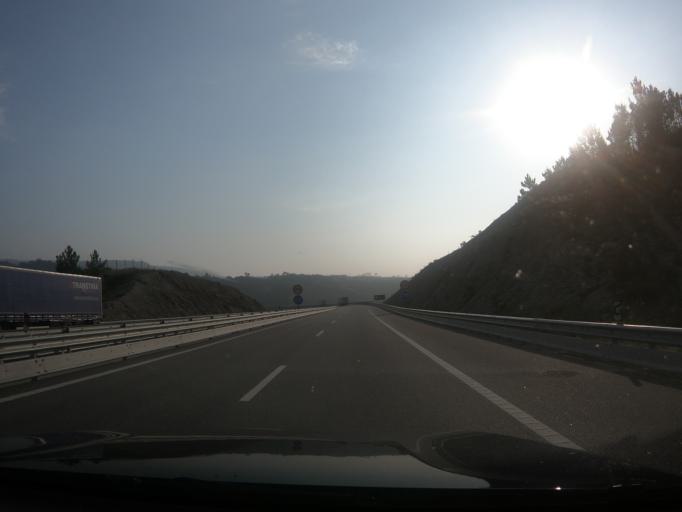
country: PT
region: Porto
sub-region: Amarante
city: Amarante
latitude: 41.2519
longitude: -7.9807
